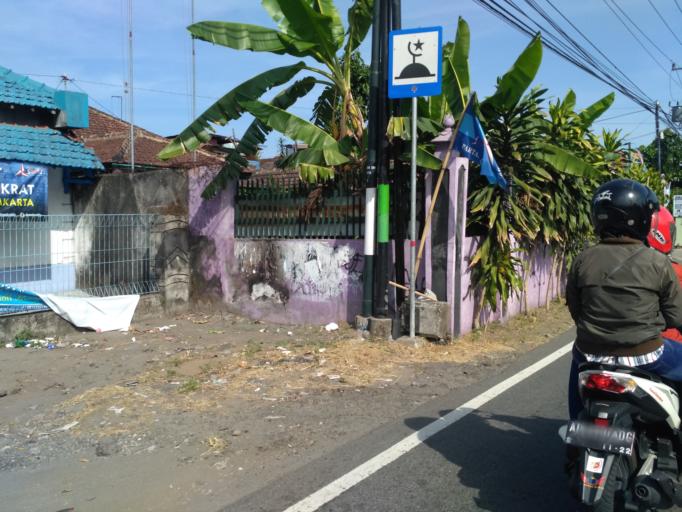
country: ID
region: Daerah Istimewa Yogyakarta
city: Depok
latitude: -7.7697
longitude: 110.4312
